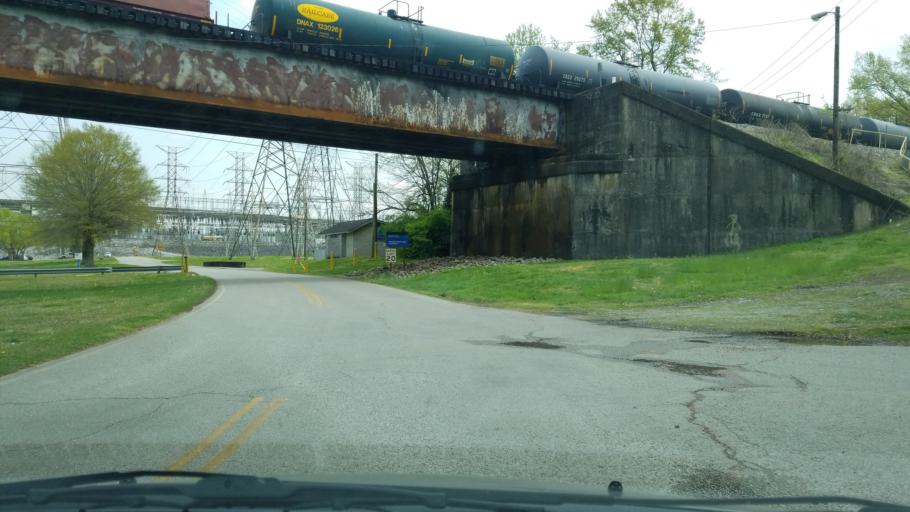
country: US
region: Tennessee
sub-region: Hamilton County
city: East Chattanooga
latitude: 35.1020
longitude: -85.2335
